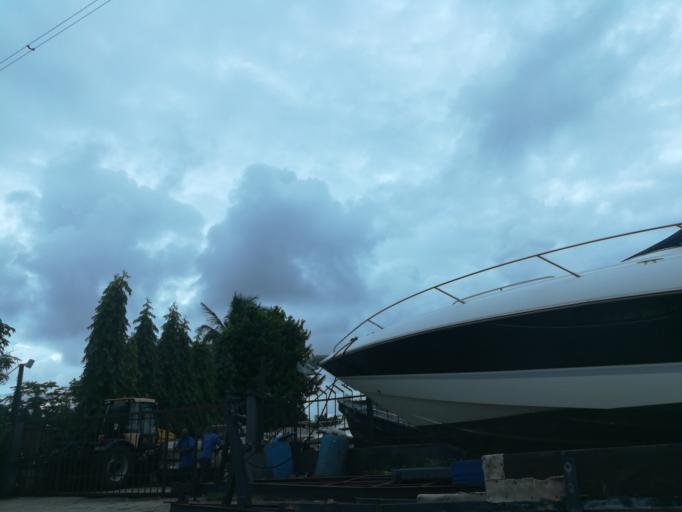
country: NG
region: Lagos
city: Ikoyi
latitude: 6.4470
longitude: 3.4540
